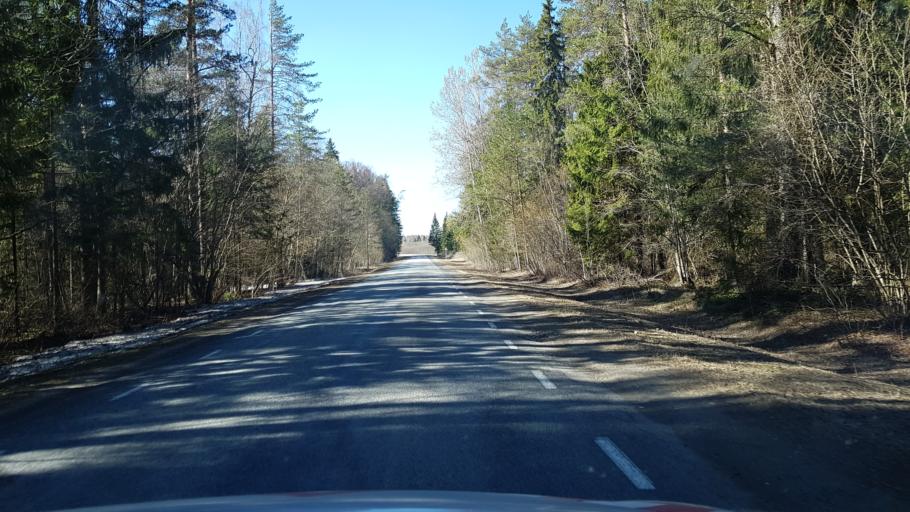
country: EE
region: Laeaene-Virumaa
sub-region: Vaeike-Maarja vald
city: Vaike-Maarja
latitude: 59.1217
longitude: 26.3134
